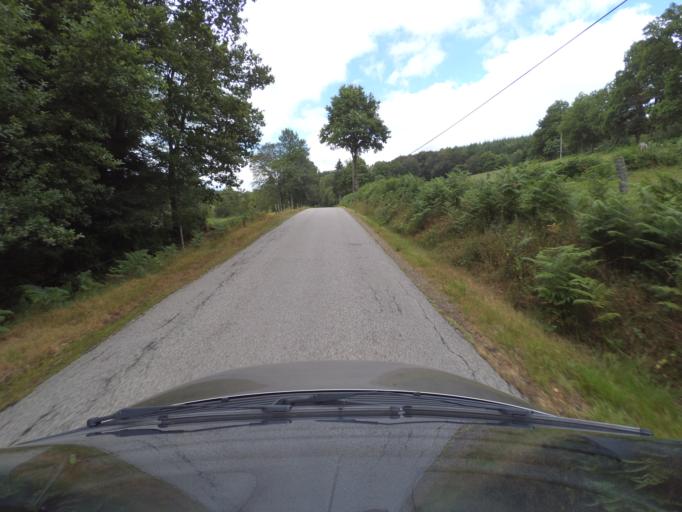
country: FR
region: Limousin
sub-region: Departement de la Creuse
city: Banize
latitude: 45.8182
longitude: 1.9250
